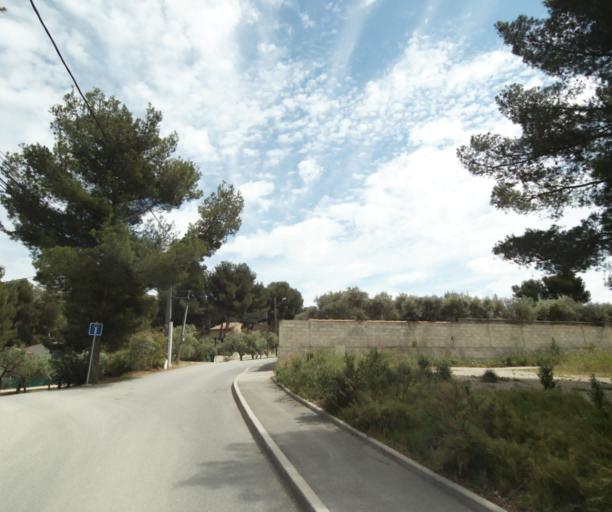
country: FR
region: Provence-Alpes-Cote d'Azur
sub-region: Departement des Bouches-du-Rhone
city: Rognac
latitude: 43.4856
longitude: 5.2427
